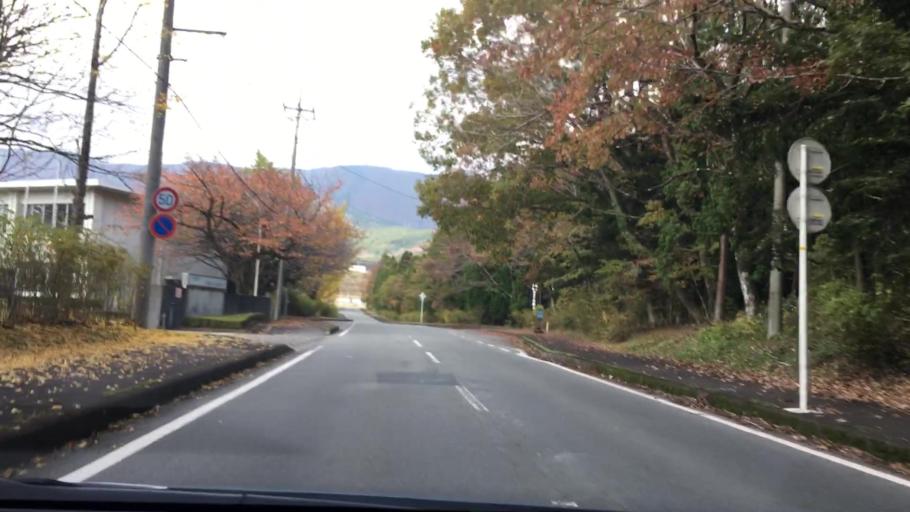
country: JP
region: Shizuoka
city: Gotemba
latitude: 35.3646
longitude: 138.9407
